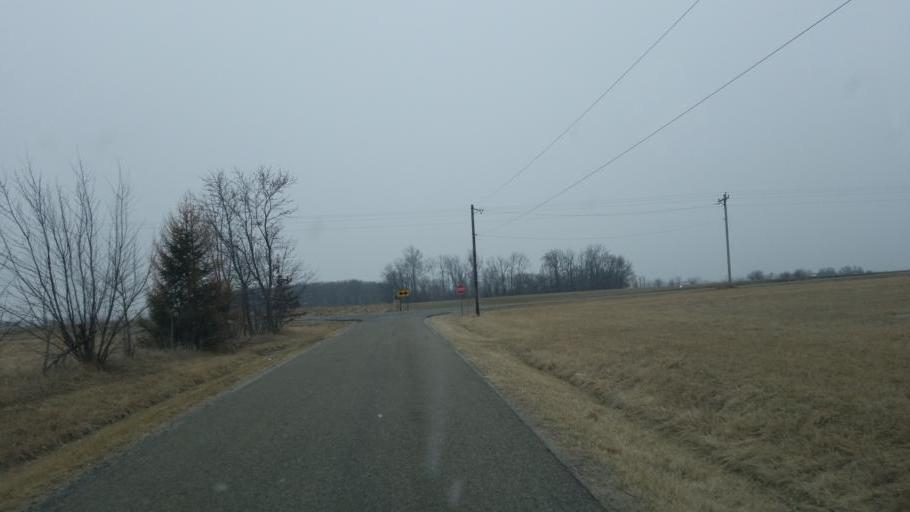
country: US
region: Ohio
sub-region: Defiance County
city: Hicksville
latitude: 41.3256
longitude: -84.7382
